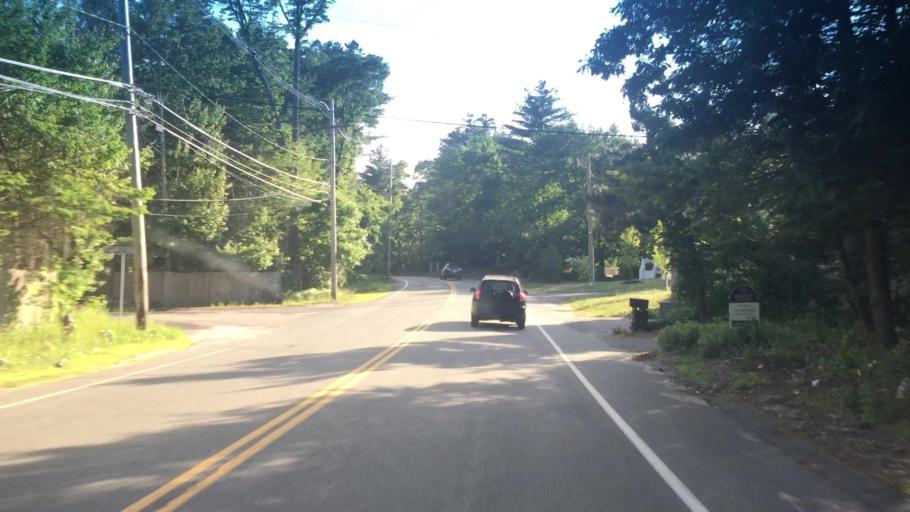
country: US
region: Massachusetts
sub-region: Norfolk County
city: Westwood
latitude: 42.2037
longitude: -71.2629
